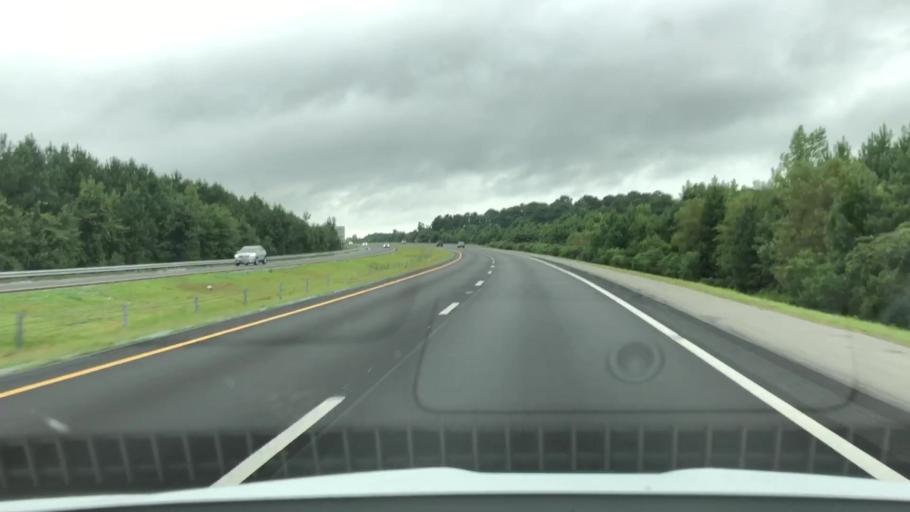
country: US
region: North Carolina
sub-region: Wayne County
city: Goldsboro
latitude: 35.4360
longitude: -77.9850
